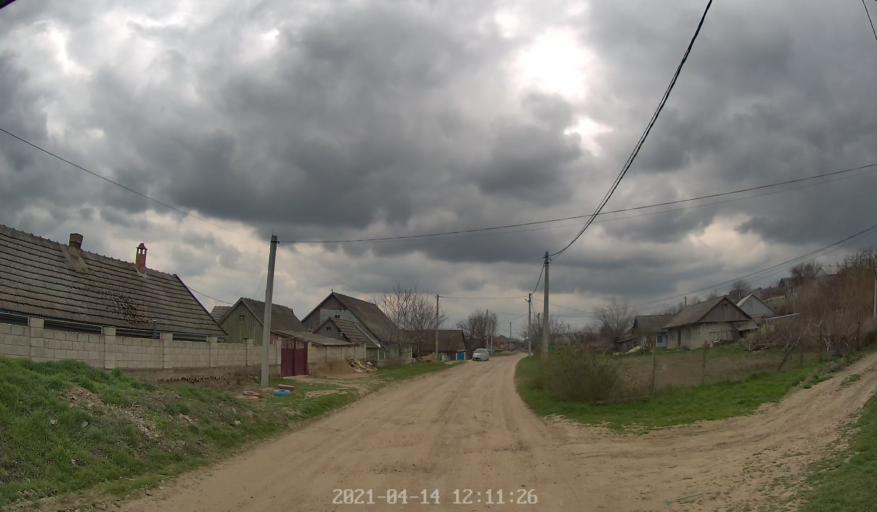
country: MD
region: Criuleni
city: Criuleni
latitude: 47.1663
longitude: 29.2034
